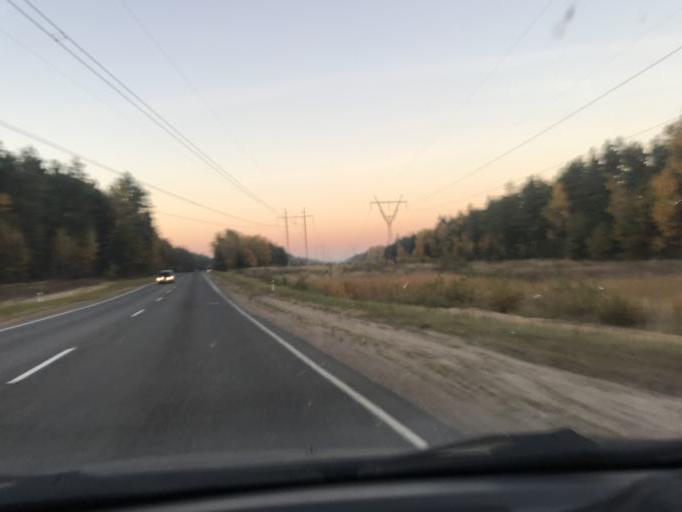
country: BY
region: Mogilev
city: Babruysk
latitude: 53.1137
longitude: 29.0542
